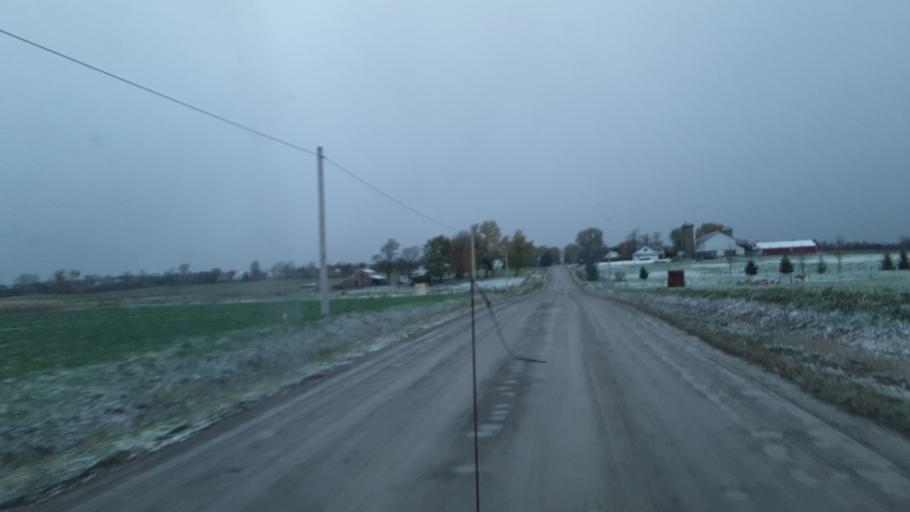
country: US
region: Ohio
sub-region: Geauga County
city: Middlefield
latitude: 41.4063
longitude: -81.0802
